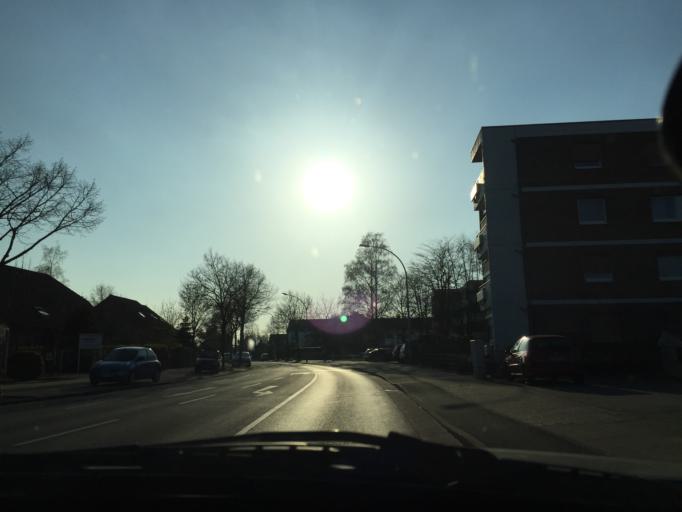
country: DE
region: North Rhine-Westphalia
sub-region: Regierungsbezirk Dusseldorf
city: Kleve
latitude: 51.7738
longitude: 6.1320
